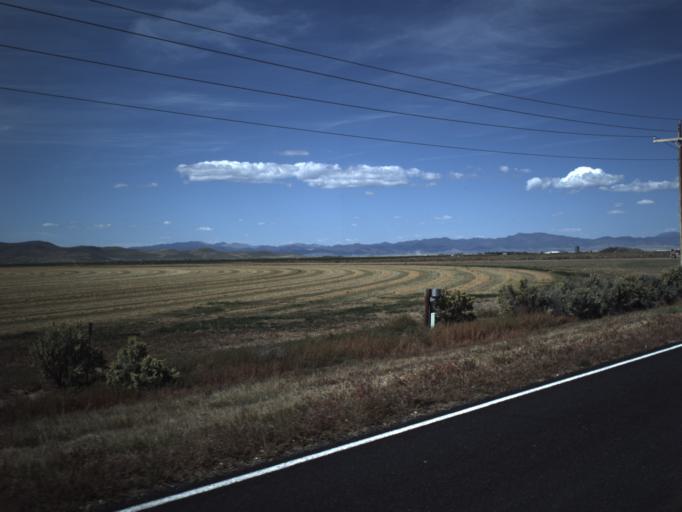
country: US
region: Utah
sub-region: Washington County
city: Enterprise
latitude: 37.6676
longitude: -113.6612
